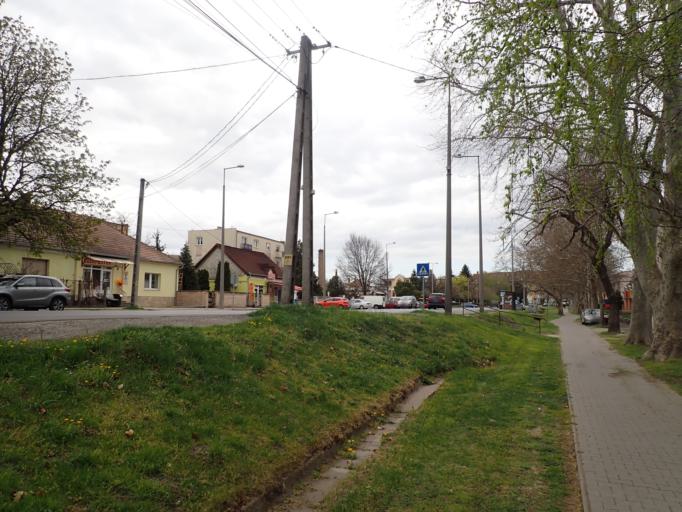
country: HU
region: Tolna
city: Paks
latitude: 46.6184
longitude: 18.8525
